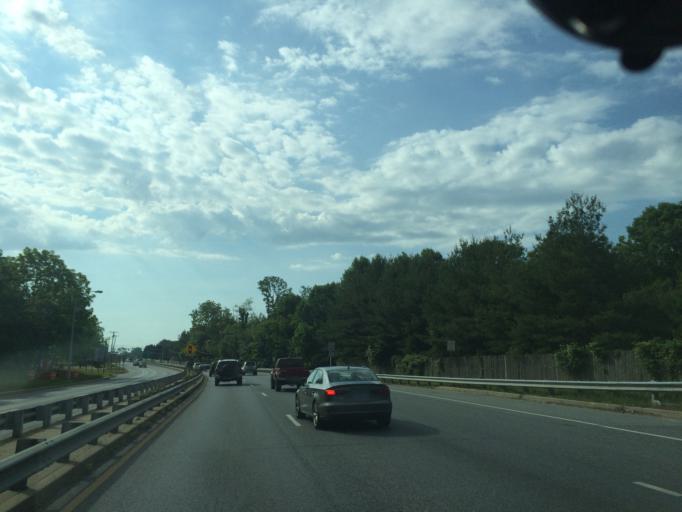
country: US
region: Maryland
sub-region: Baltimore County
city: Reisterstown
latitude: 39.4814
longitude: -76.8563
